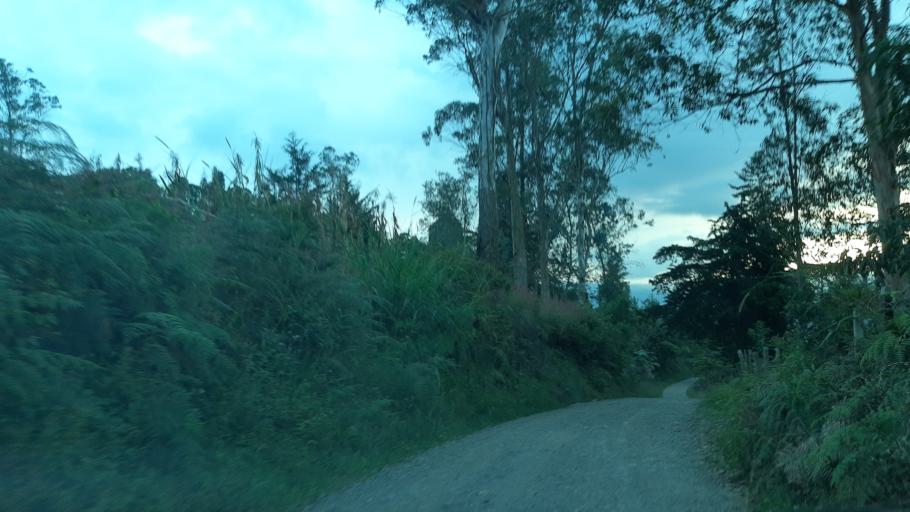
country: CO
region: Boyaca
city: Garagoa
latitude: 5.1098
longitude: -73.3541
